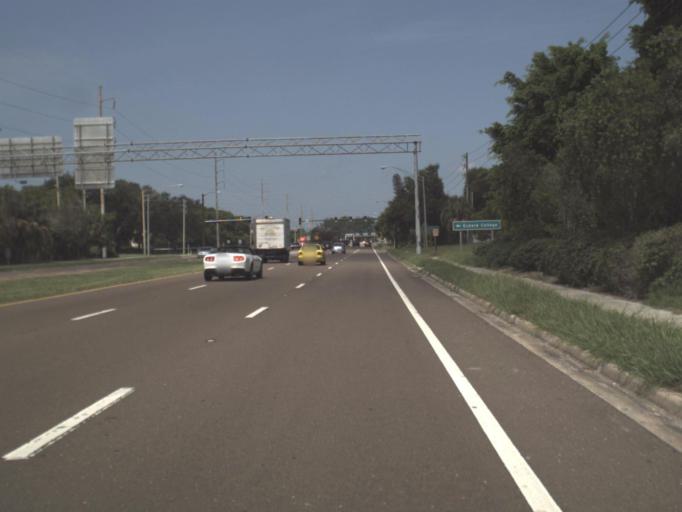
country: US
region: Florida
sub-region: Pinellas County
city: Gulfport
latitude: 27.7192
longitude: -82.6862
